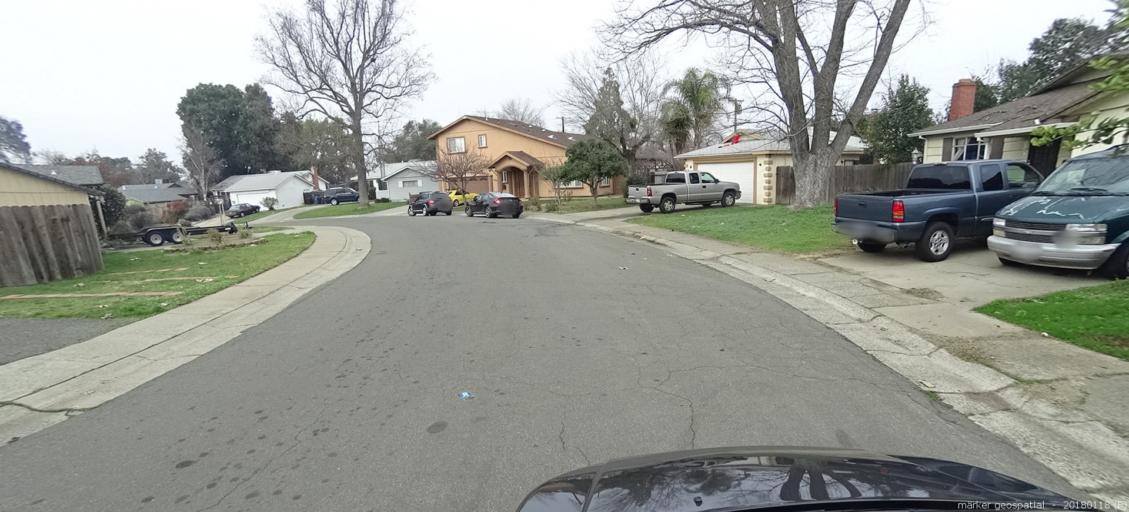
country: US
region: California
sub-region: Sacramento County
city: Rancho Cordova
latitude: 38.5977
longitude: -121.3108
